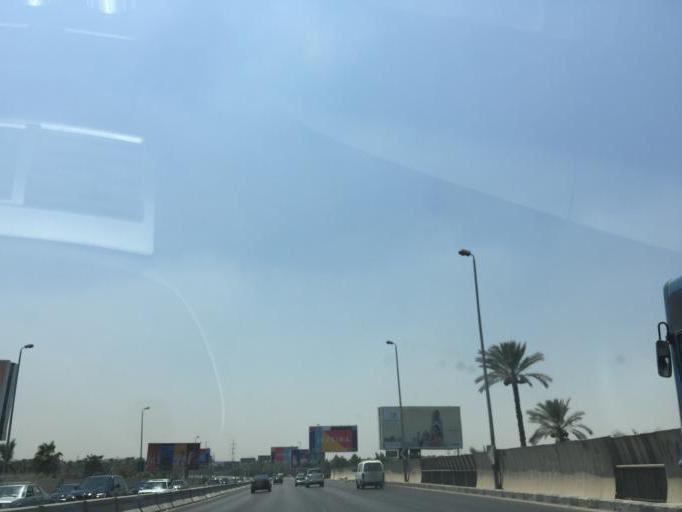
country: EG
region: Al Jizah
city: Awsim
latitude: 30.0628
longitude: 31.0959
